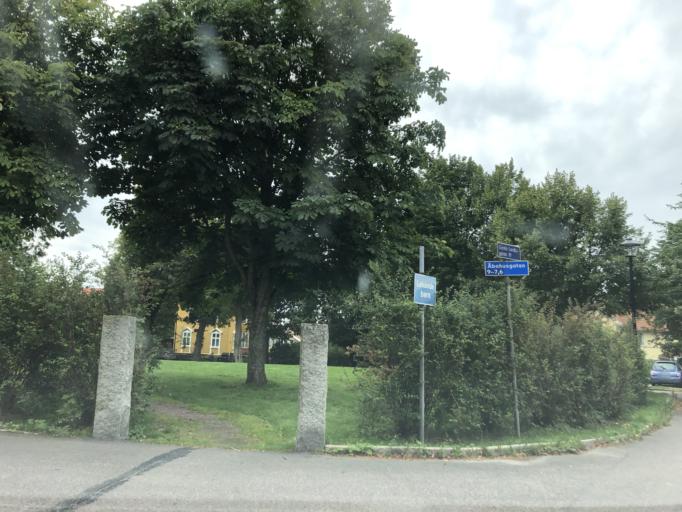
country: SE
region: Vaestra Goetaland
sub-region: Goteborg
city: Majorna
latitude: 57.7113
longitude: 11.9147
